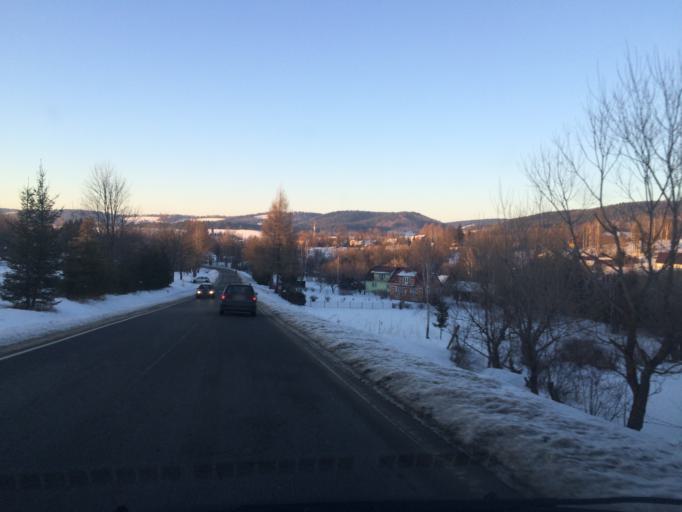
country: PL
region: Subcarpathian Voivodeship
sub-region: Powiat bieszczadzki
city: Czarna
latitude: 49.3174
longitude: 22.6728
